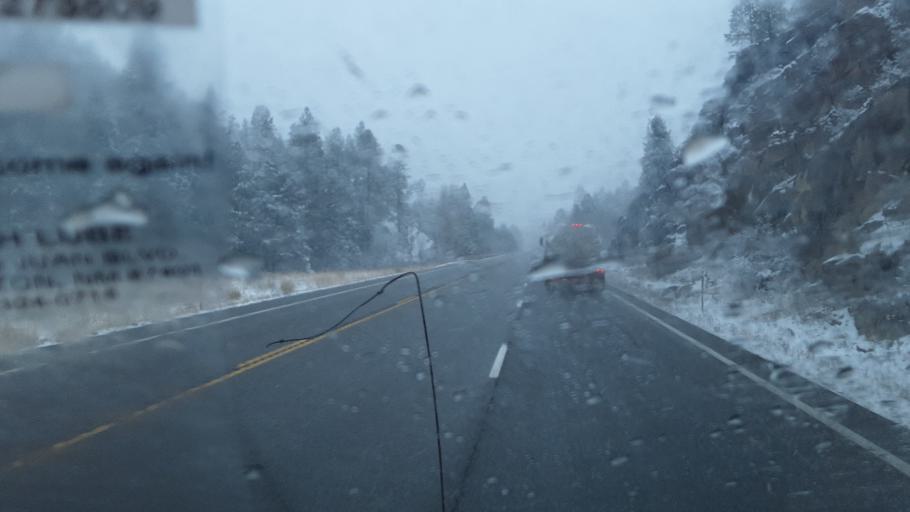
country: US
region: Colorado
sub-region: La Plata County
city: Bayfield
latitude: 37.2326
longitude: -107.4192
